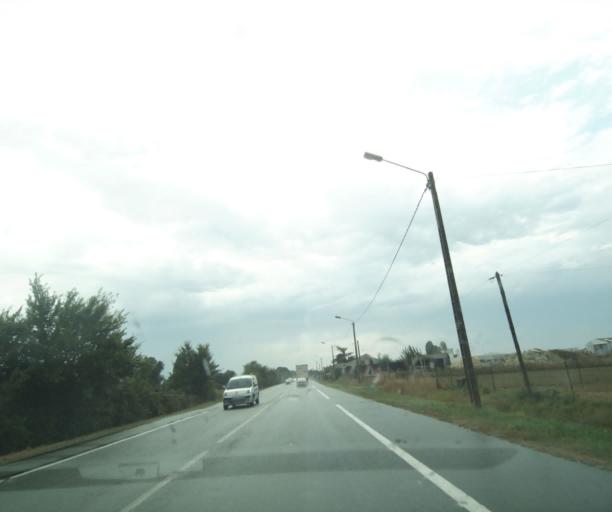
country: FR
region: Poitou-Charentes
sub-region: Departement de la Charente-Maritime
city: Tonnay-Charente
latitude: 45.9523
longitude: -0.8849
